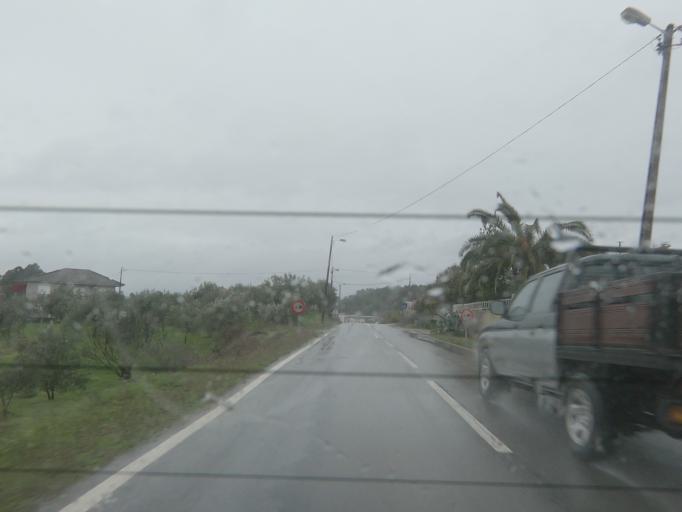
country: PT
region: Vila Real
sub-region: Sabrosa
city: Vilela
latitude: 41.2358
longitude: -7.6821
